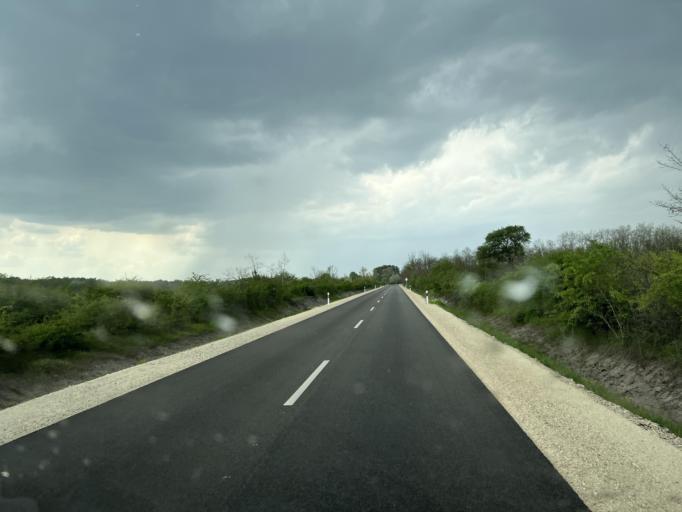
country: HU
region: Pest
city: Csemo
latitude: 47.0631
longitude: 19.7059
